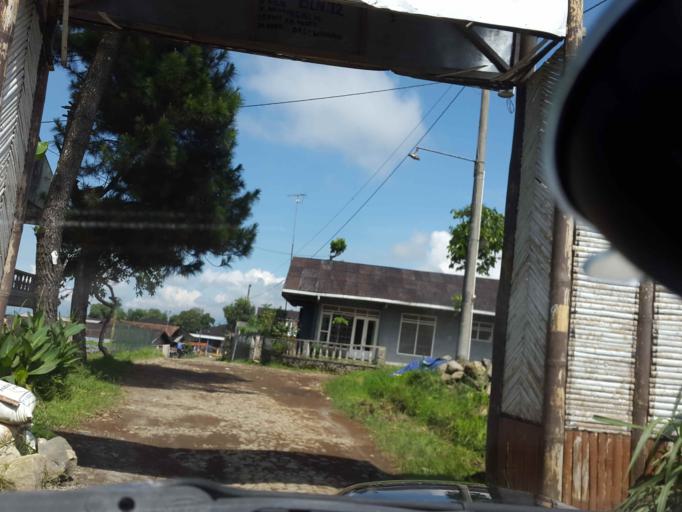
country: ID
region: Central Java
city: Wonosobo
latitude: -7.3996
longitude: 110.0228
